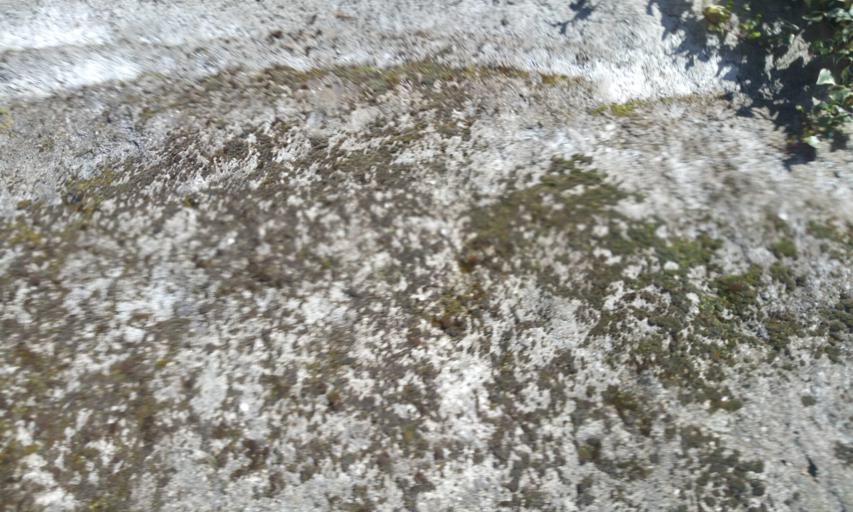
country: PT
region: Guarda
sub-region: Seia
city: Seia
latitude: 40.4672
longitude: -7.6221
